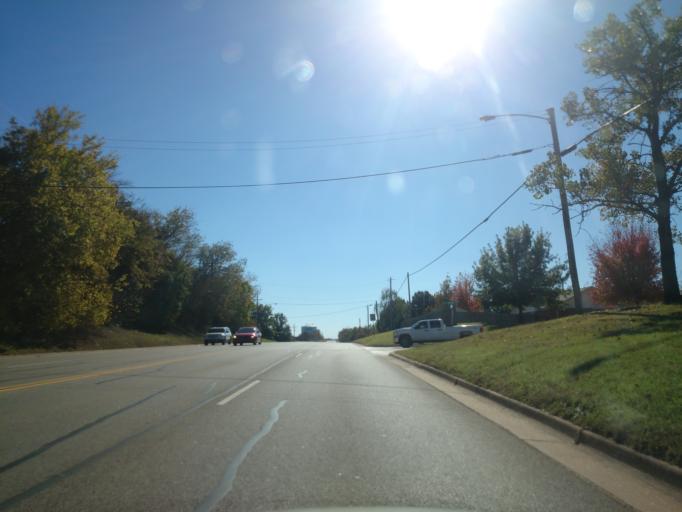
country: US
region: Oklahoma
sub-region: Payne County
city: Stillwater
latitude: 36.1562
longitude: -97.0698
